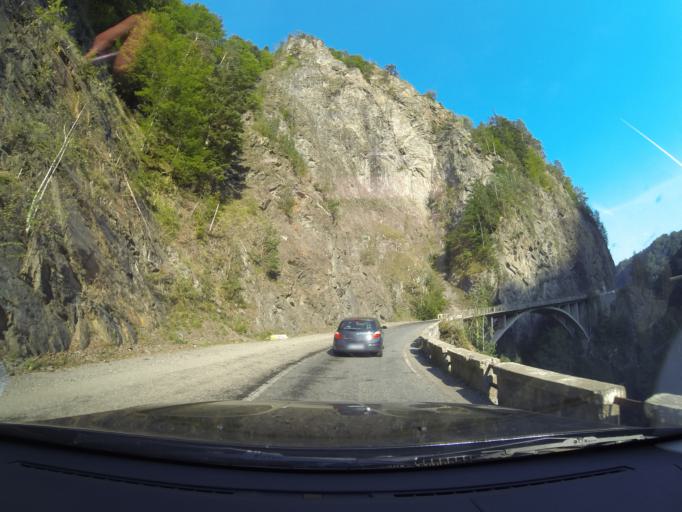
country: RO
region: Arges
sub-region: Comuna Arefu
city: Arefu
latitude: 45.3600
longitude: 24.6315
